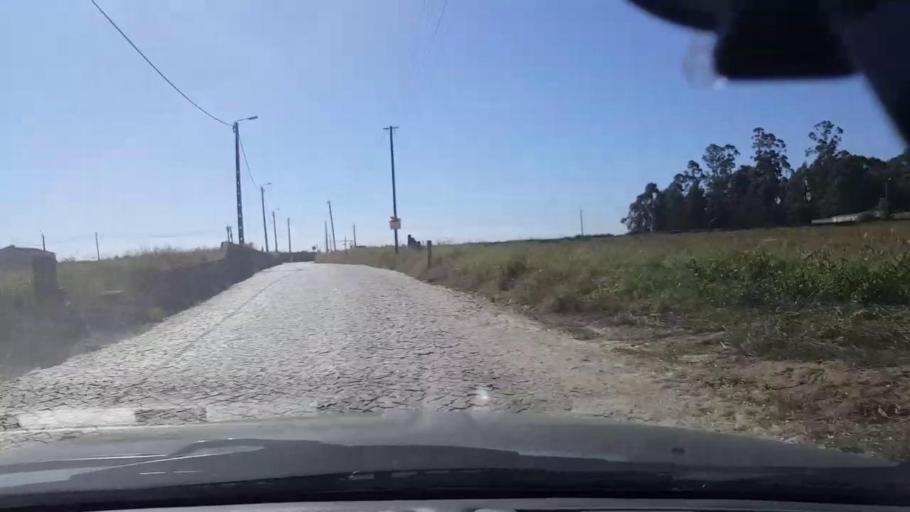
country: PT
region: Porto
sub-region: Maia
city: Gemunde
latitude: 41.2915
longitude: -8.6677
